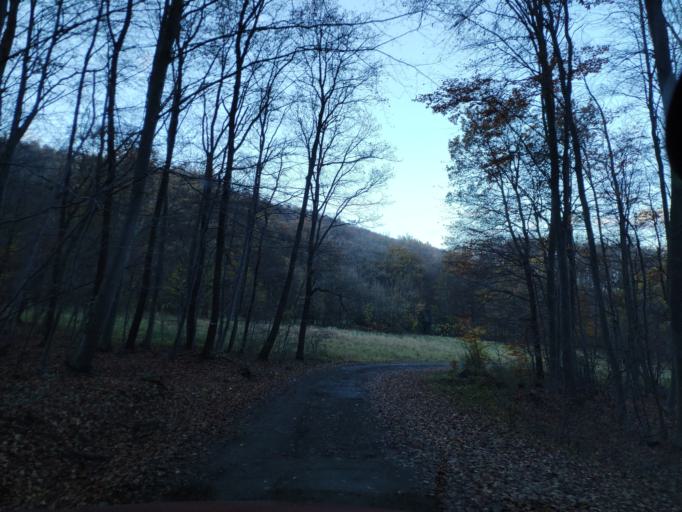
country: SK
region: Kosicky
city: Secovce
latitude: 48.5858
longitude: 21.5053
